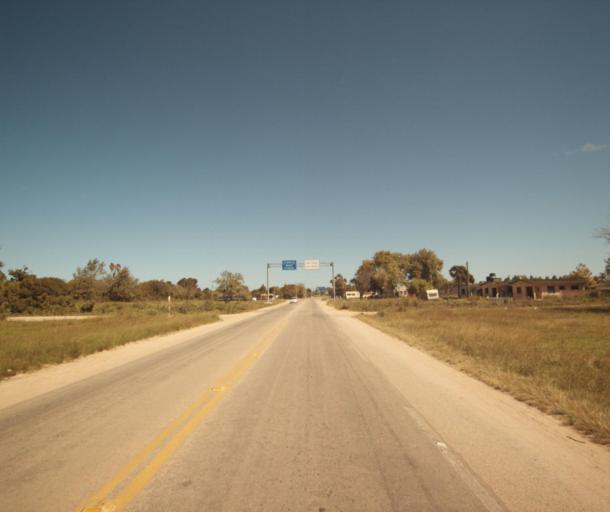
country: BR
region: Rio Grande do Sul
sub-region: Chui
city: Chui
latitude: -33.6915
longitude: -53.4472
